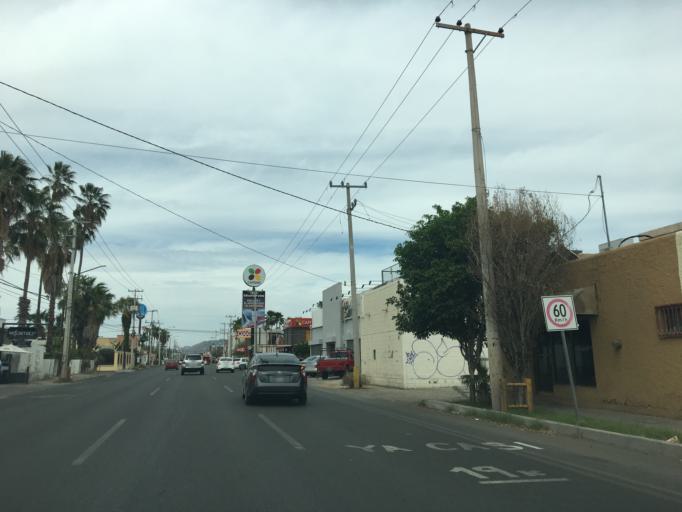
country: MX
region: Sonora
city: Hermosillo
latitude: 29.0742
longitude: -110.9653
